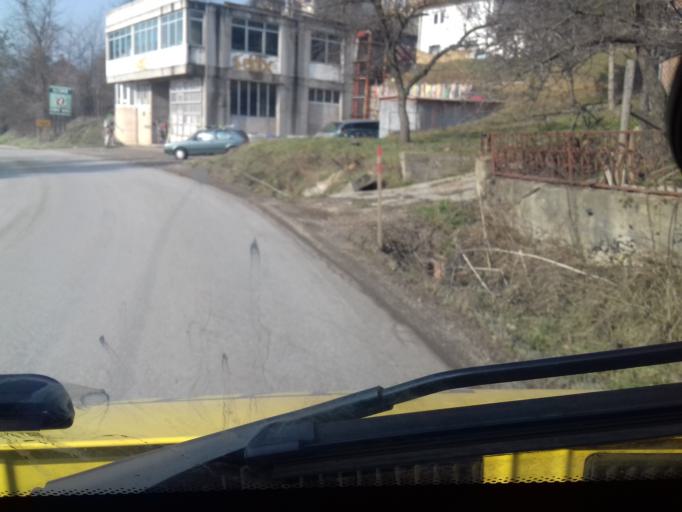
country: BA
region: Federation of Bosnia and Herzegovina
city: Ilijas
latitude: 43.9454
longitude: 18.2693
